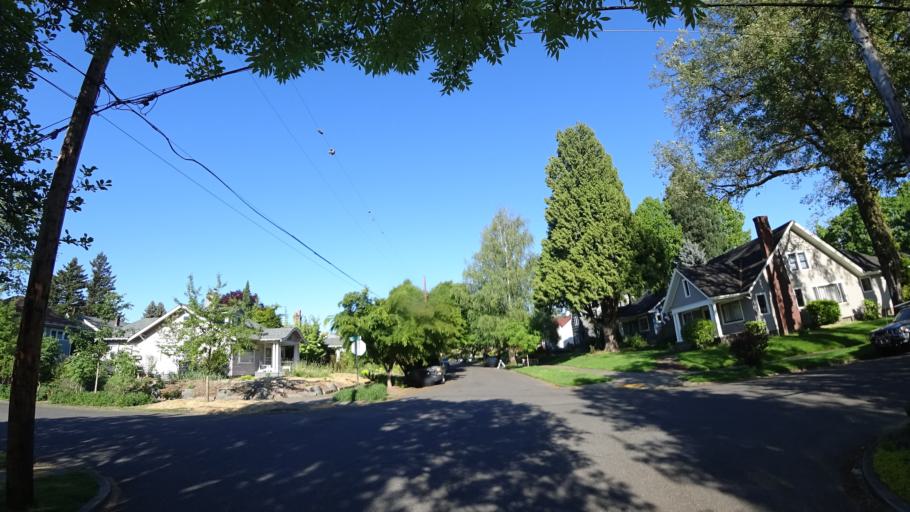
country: US
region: Oregon
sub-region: Multnomah County
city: Portland
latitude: 45.5286
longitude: -122.6308
